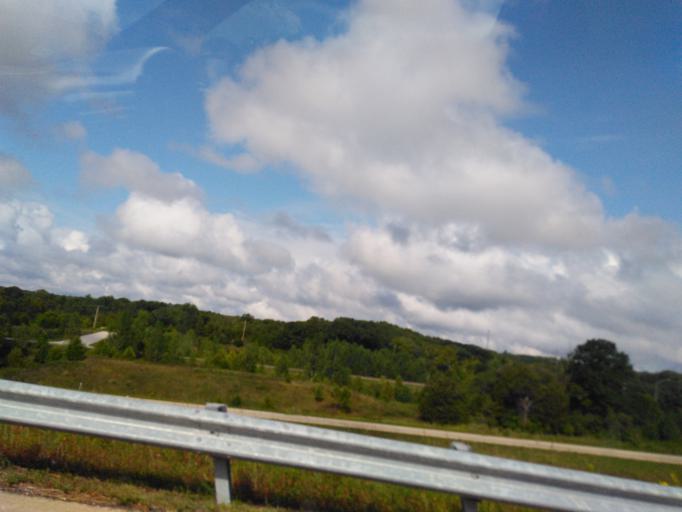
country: US
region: Missouri
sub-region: Jefferson County
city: Hillsboro
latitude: 38.2682
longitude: -90.5530
